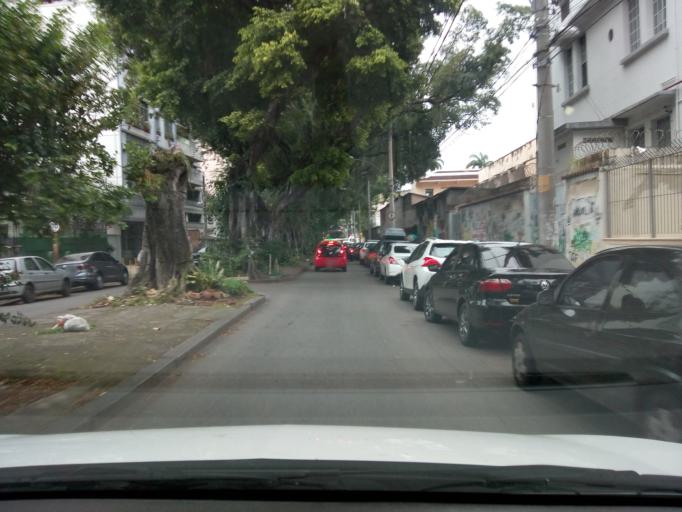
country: BR
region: Rio de Janeiro
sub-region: Rio De Janeiro
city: Rio de Janeiro
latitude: -22.9142
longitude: -43.2272
